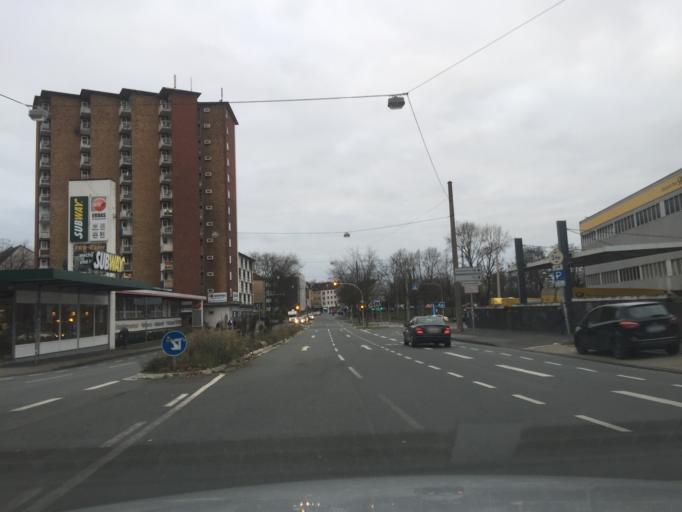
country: DE
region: North Rhine-Westphalia
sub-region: Regierungsbezirk Dusseldorf
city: Oberhausen
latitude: 51.4733
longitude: 6.8526
